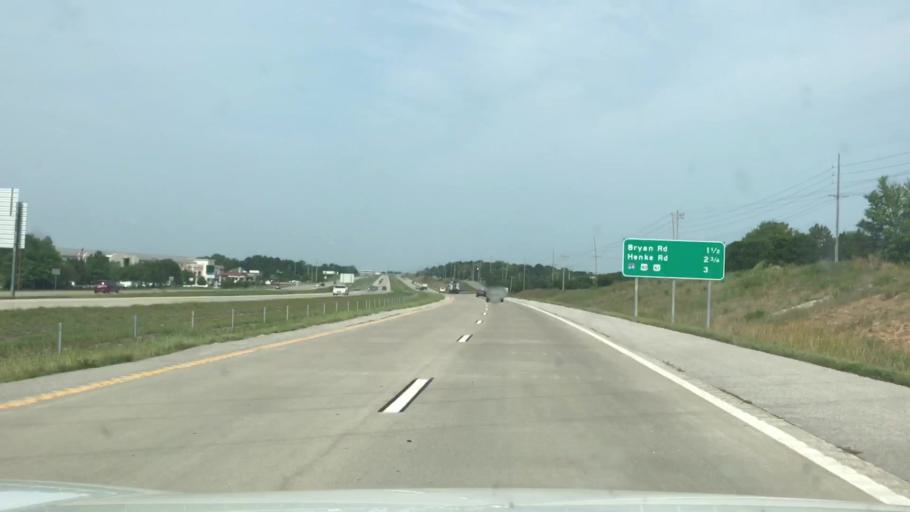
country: US
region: Missouri
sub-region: Saint Charles County
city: Dardenne Prairie
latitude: 38.7591
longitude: -90.7134
